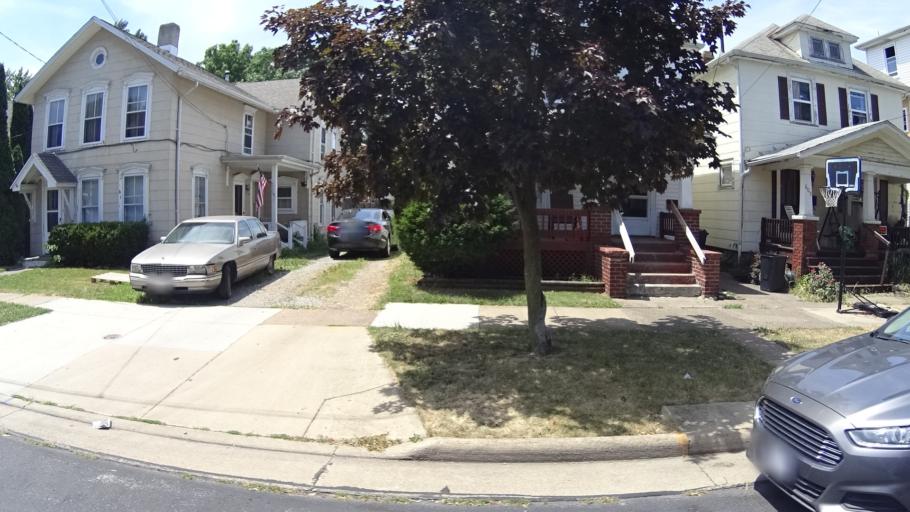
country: US
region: Ohio
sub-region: Erie County
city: Sandusky
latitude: 41.4480
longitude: -82.7182
